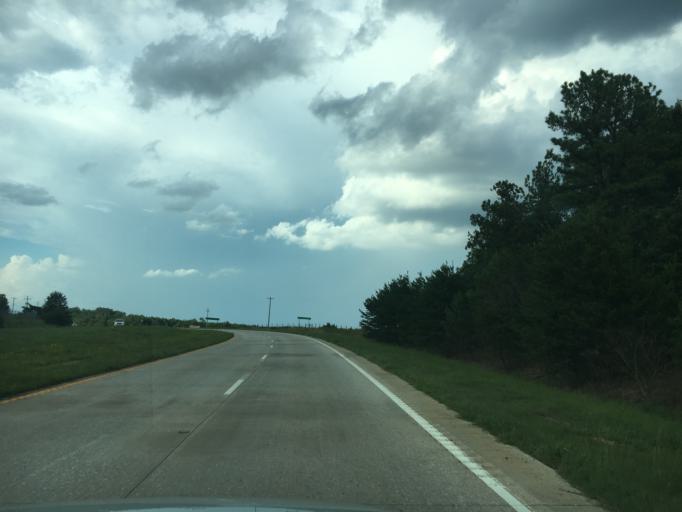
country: US
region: South Carolina
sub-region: Greenville County
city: Greer
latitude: 34.9007
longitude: -82.2203
